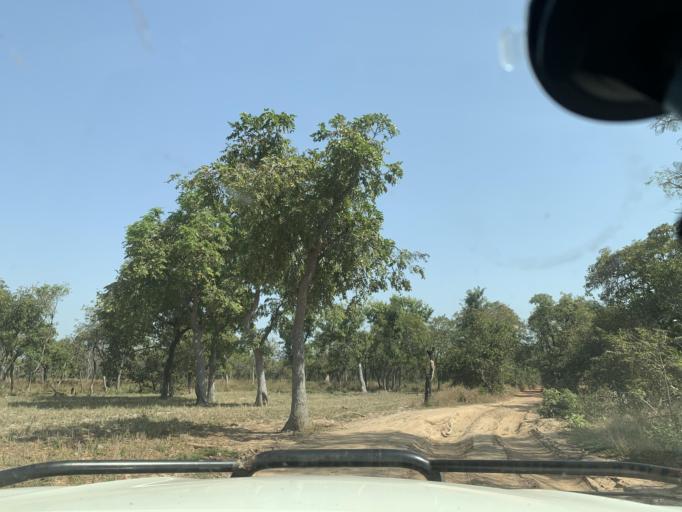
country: ML
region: Sikasso
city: Kolondieba
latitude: 10.8930
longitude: -6.7492
